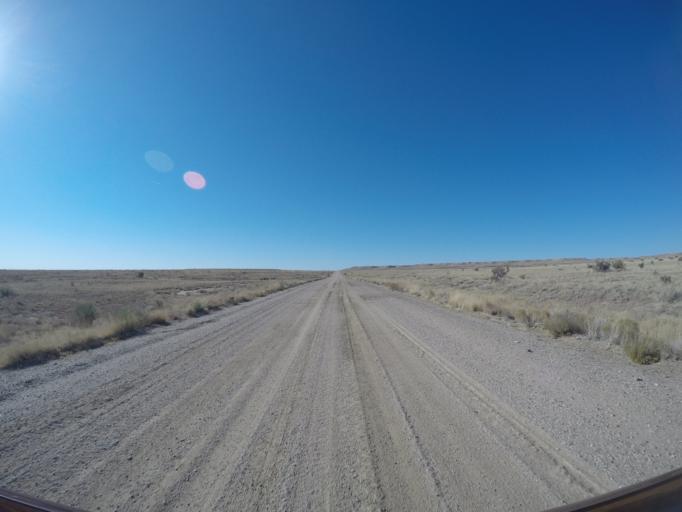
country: US
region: Colorado
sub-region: Otero County
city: La Junta
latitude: 37.7729
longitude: -103.5582
